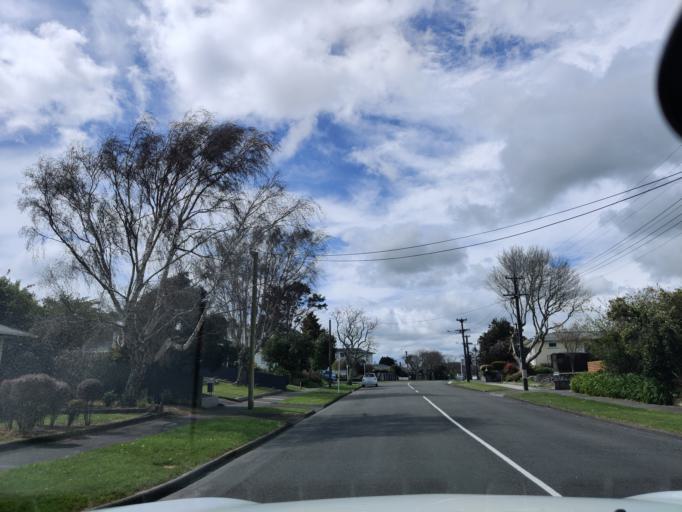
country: NZ
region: Manawatu-Wanganui
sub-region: Palmerston North City
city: Palmerston North
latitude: -40.3809
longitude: 175.5871
